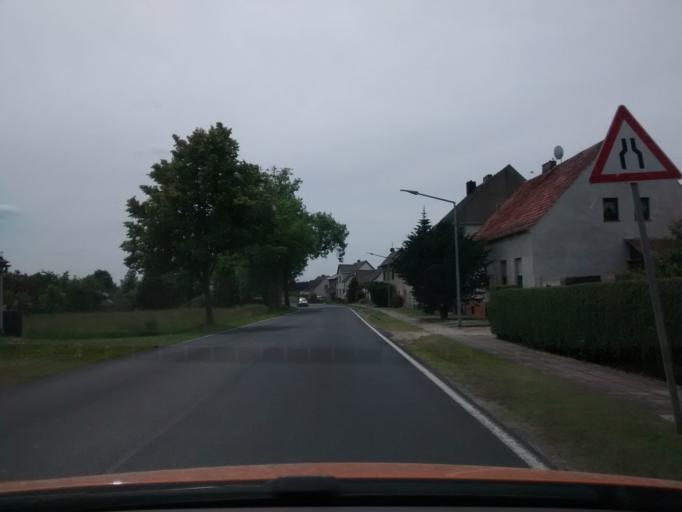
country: DE
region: Brandenburg
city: Juterbog
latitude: 51.9004
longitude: 13.1409
